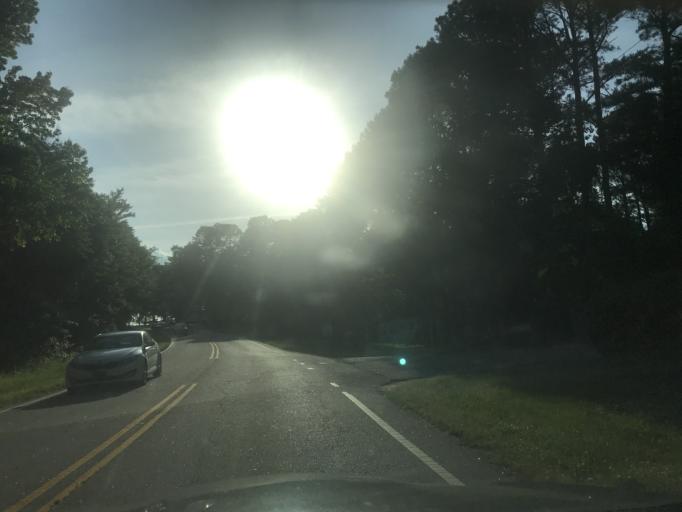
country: US
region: North Carolina
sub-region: Wake County
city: Knightdale
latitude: 35.7550
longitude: -78.5129
